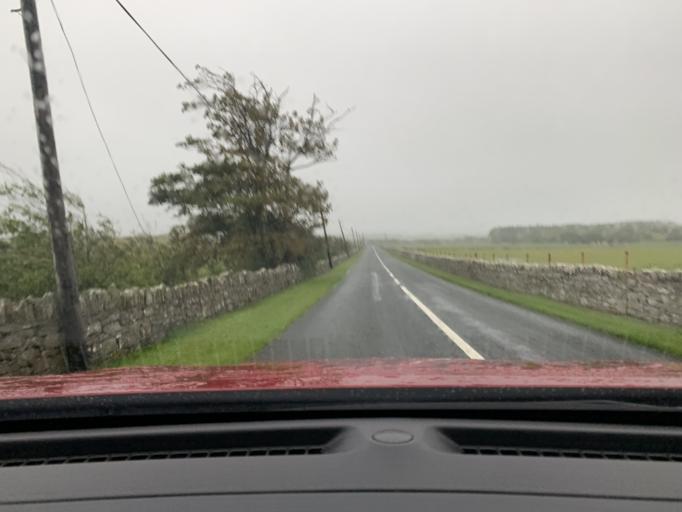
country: IE
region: Connaught
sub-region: County Leitrim
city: Kinlough
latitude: 54.4564
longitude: -8.4554
